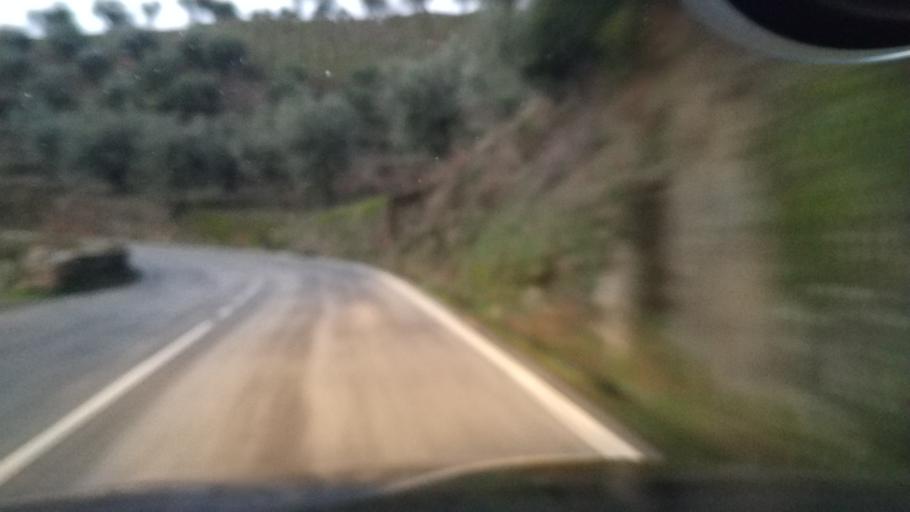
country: PT
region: Vila Real
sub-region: Santa Marta de Penaguiao
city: Santa Marta de Penaguiao
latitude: 41.2449
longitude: -7.7674
